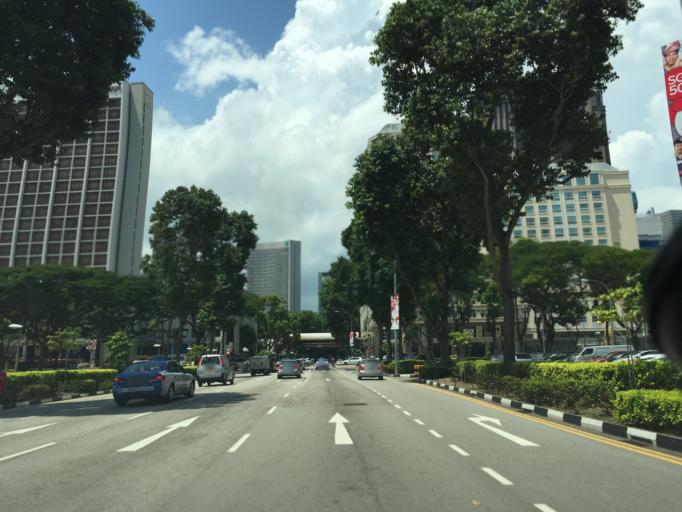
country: SG
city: Singapore
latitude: 1.3025
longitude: 103.8561
